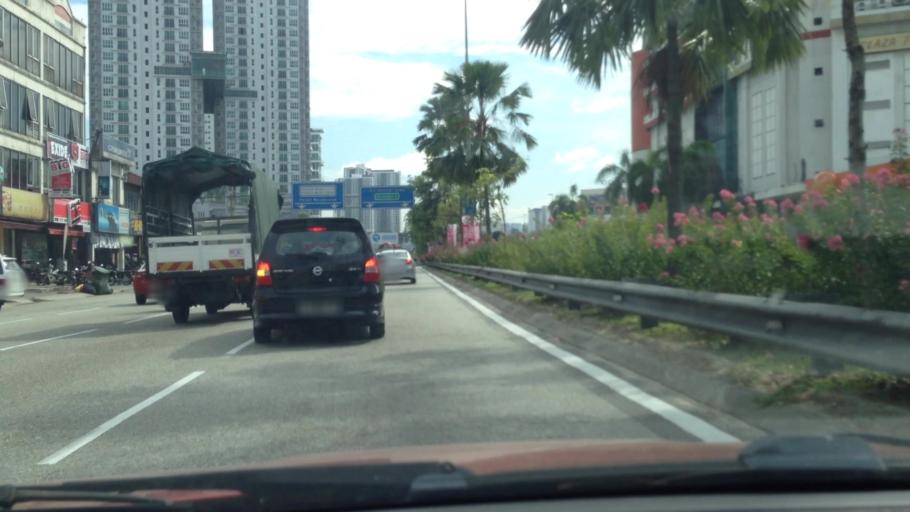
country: MY
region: Kuala Lumpur
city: Kuala Lumpur
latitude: 3.0894
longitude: 101.6743
